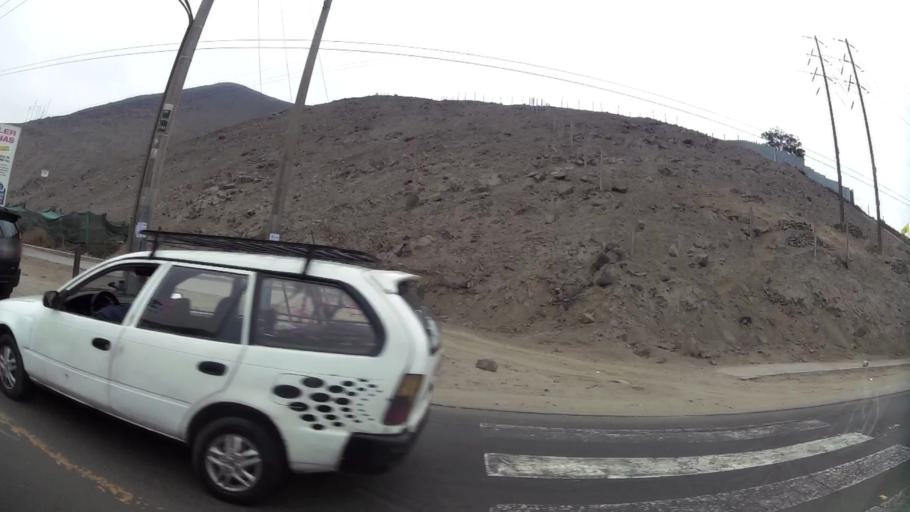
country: PE
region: Lima
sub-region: Lima
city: La Molina
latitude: -12.0855
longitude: -76.9180
